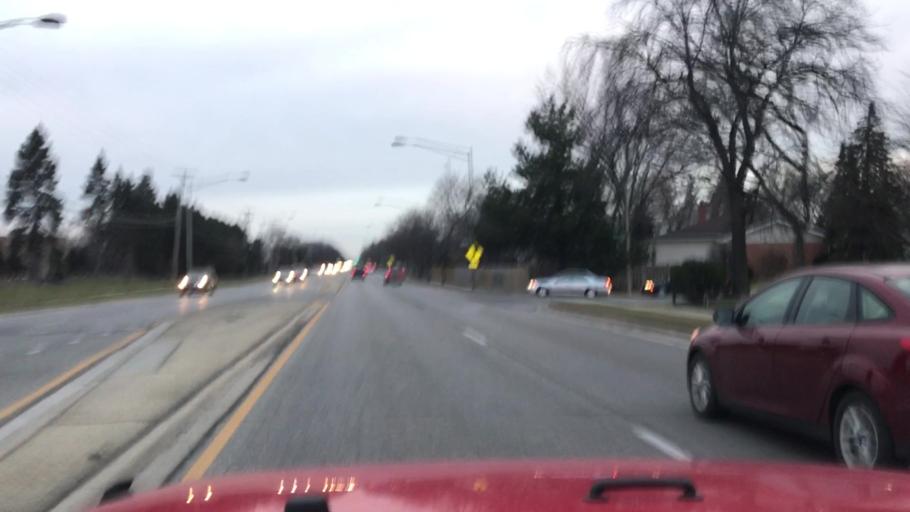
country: US
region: Illinois
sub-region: Cook County
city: Arlington Heights
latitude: 42.1144
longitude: -87.9804
